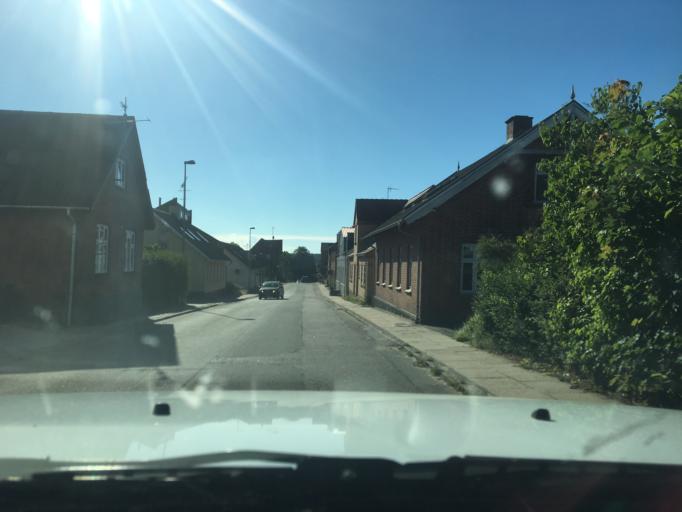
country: DK
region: Central Jutland
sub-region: Syddjurs Kommune
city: Hornslet
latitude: 56.3202
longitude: 10.3107
